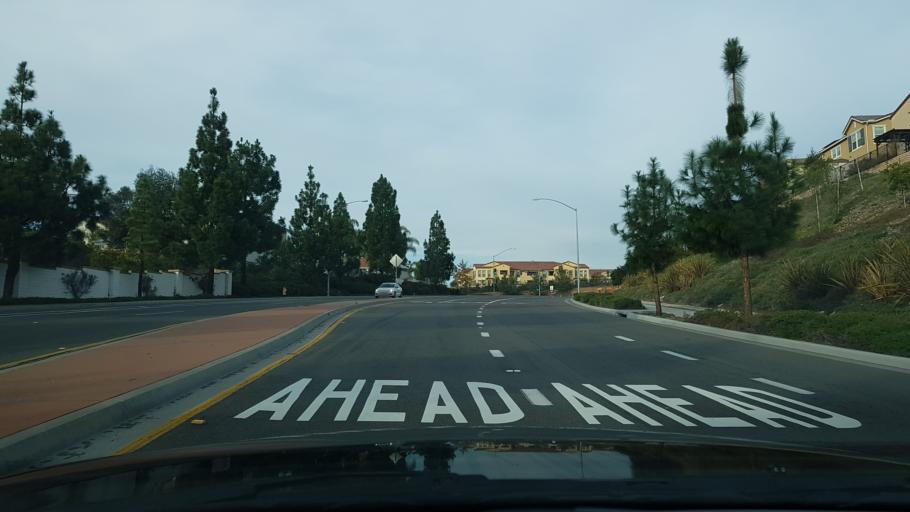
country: US
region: California
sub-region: San Diego County
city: Fairbanks Ranch
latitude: 32.9171
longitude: -117.1784
